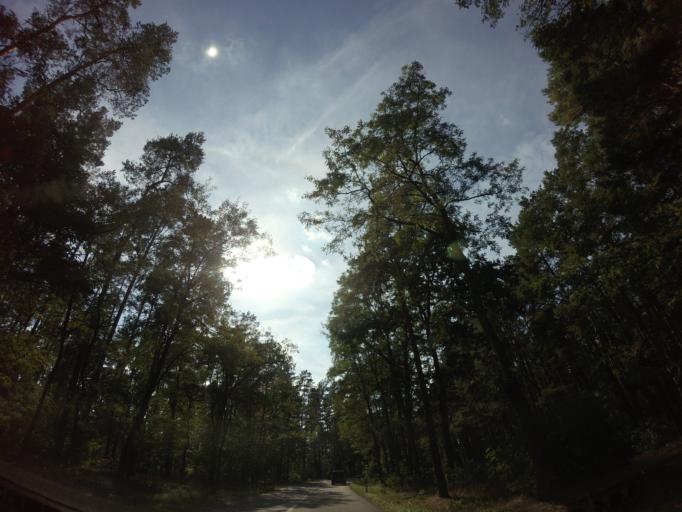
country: DE
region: Brandenburg
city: Rheinsberg
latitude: 53.1017
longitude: 12.9422
